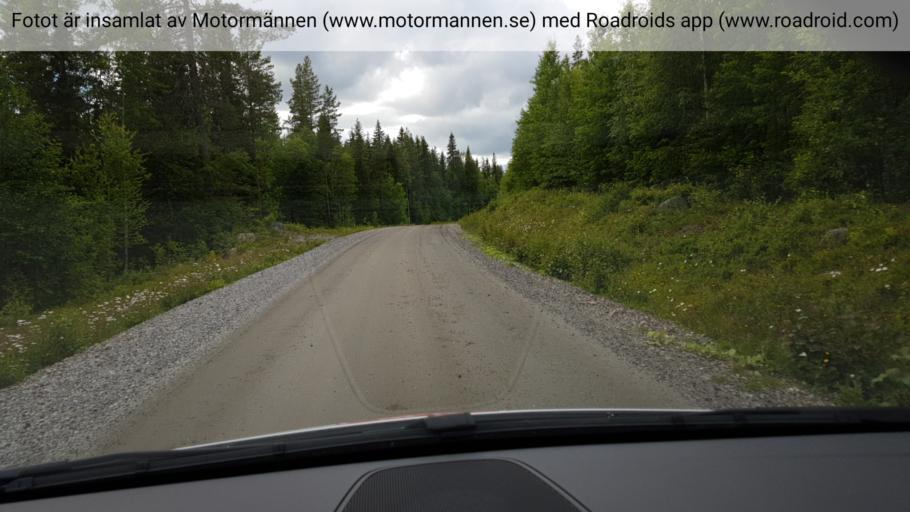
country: SE
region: Vaesterbotten
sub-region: Dorotea Kommun
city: Dorotea
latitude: 63.9290
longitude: 16.1257
